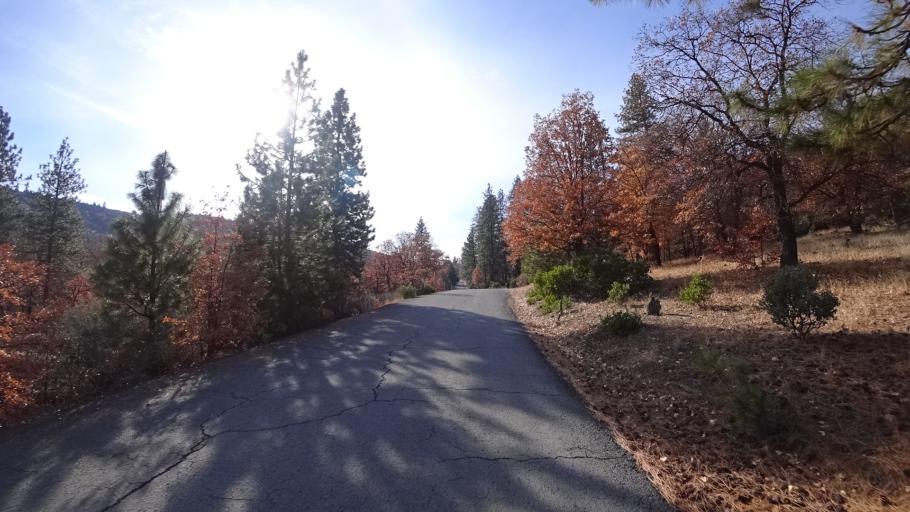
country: US
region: California
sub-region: Siskiyou County
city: Montague
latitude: 41.6174
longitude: -122.5780
